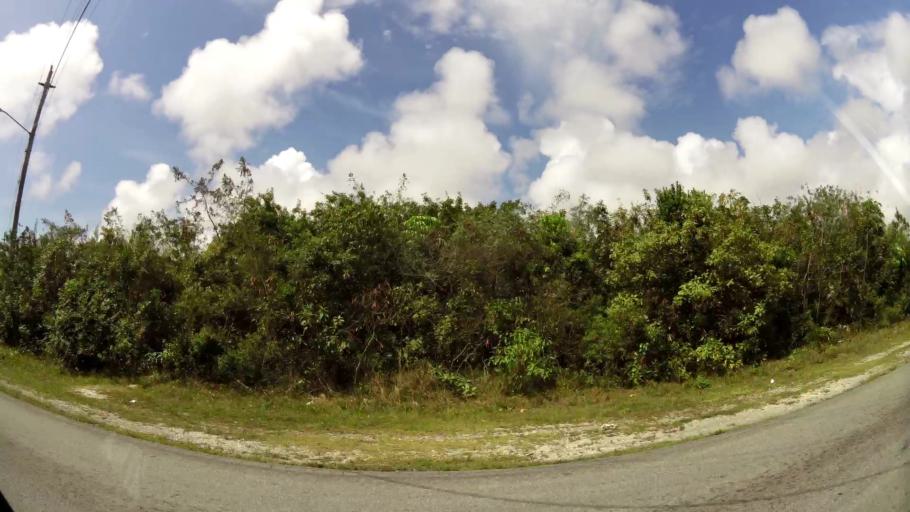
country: BS
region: Freeport
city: Freeport
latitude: 26.5113
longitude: -78.6937
